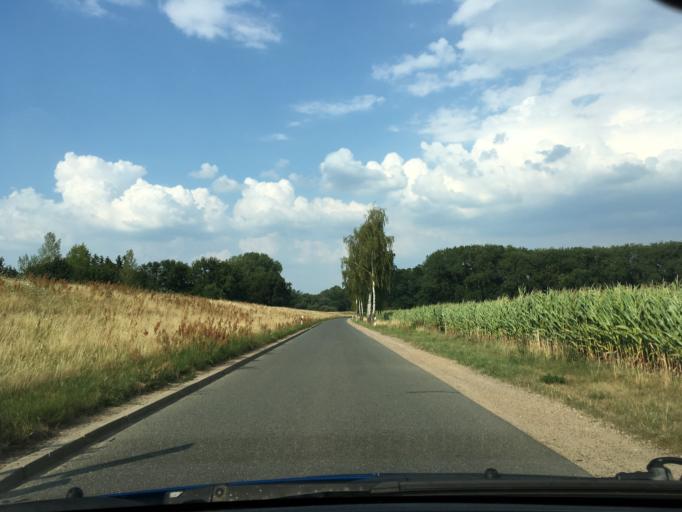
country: DE
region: Lower Saxony
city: Damnatz
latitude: 53.1586
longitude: 11.1316
